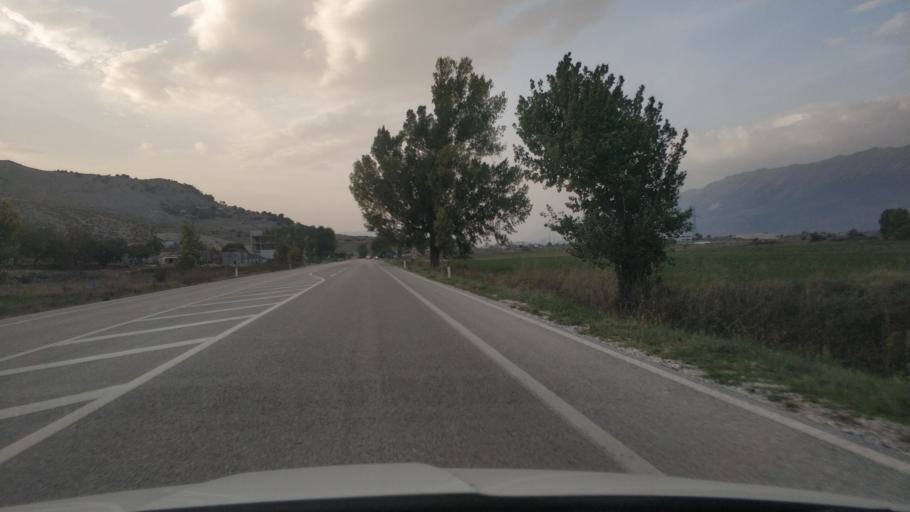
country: AL
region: Gjirokaster
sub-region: Rrethi i Gjirokastres
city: Libohove
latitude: 39.9656
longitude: 20.2409
